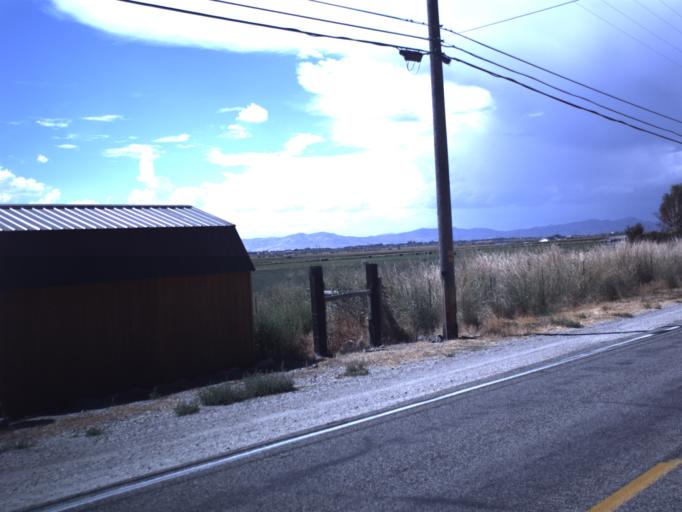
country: US
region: Utah
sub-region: Box Elder County
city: Honeyville
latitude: 41.5820
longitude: -112.0369
